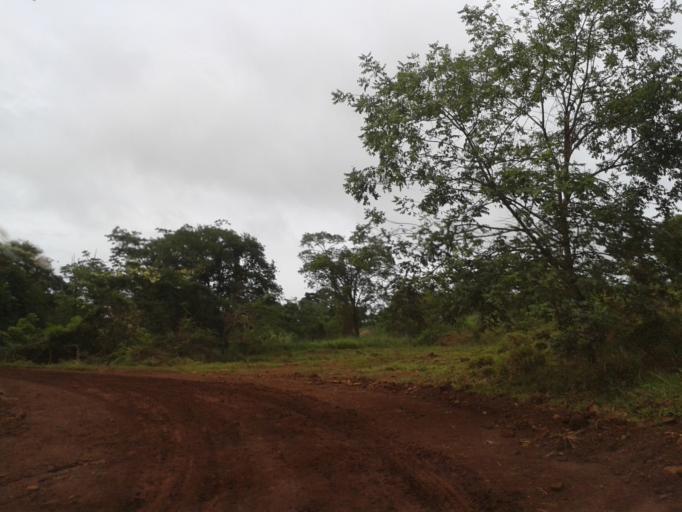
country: BR
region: Minas Gerais
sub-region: Capinopolis
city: Capinopolis
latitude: -18.7386
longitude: -49.7746
